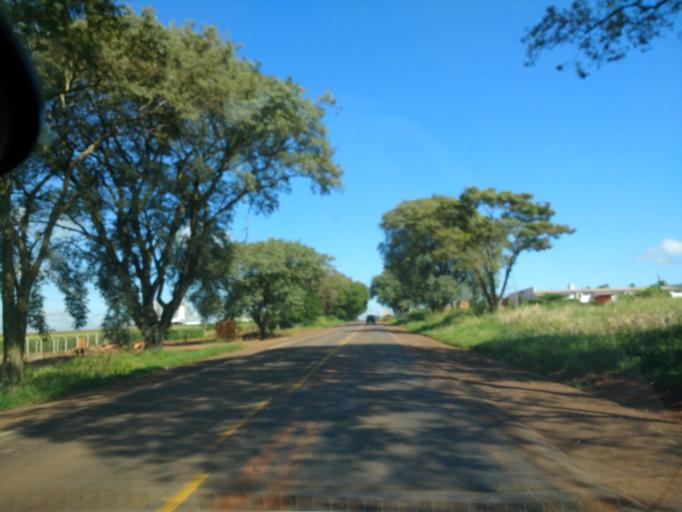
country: BR
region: Parana
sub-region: Terra Boa
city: Terra Boa
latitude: -23.6305
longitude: -52.4589
